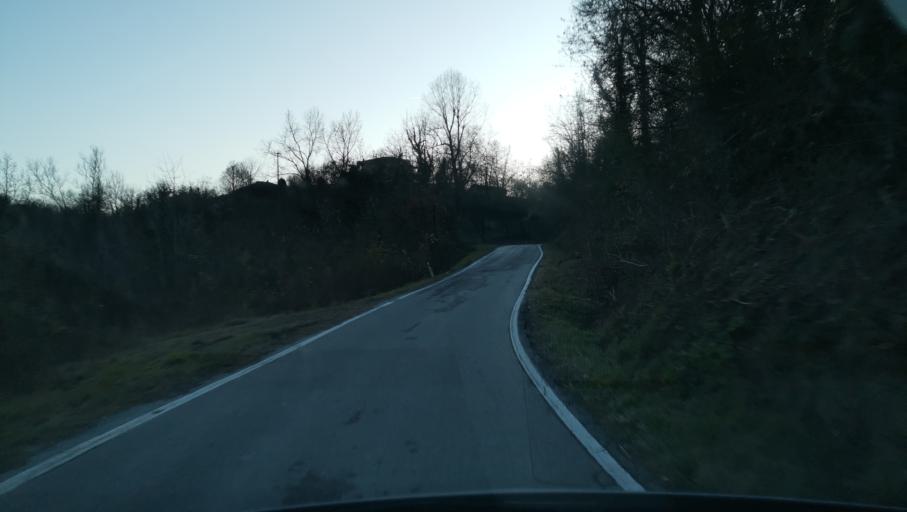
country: IT
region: Piedmont
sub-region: Provincia di Torino
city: Cinzano
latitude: 45.1084
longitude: 7.9273
